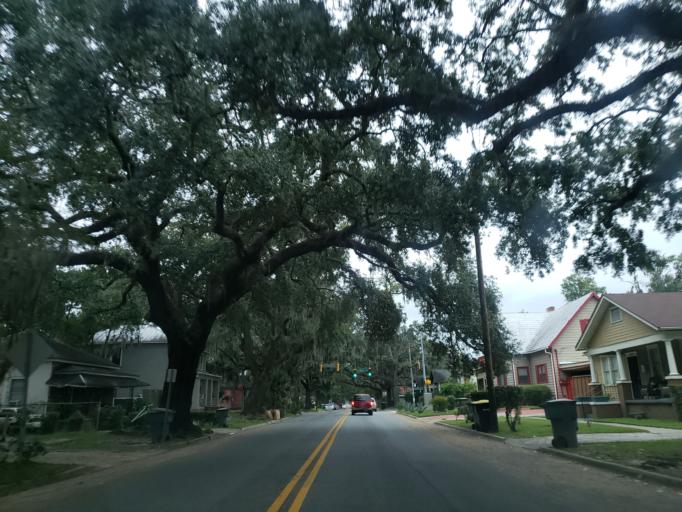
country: US
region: Georgia
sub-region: Chatham County
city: Savannah
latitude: 32.0536
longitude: -81.0869
